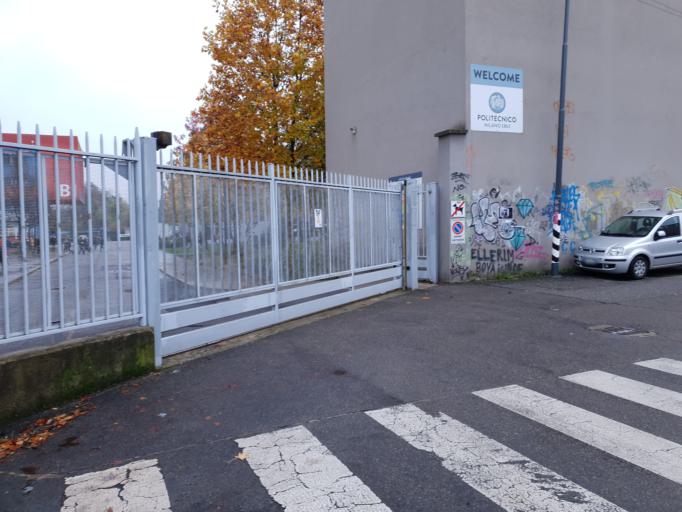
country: IT
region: Lombardy
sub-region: Citta metropolitana di Milano
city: Novate Milanese
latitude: 45.5061
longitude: 9.1660
